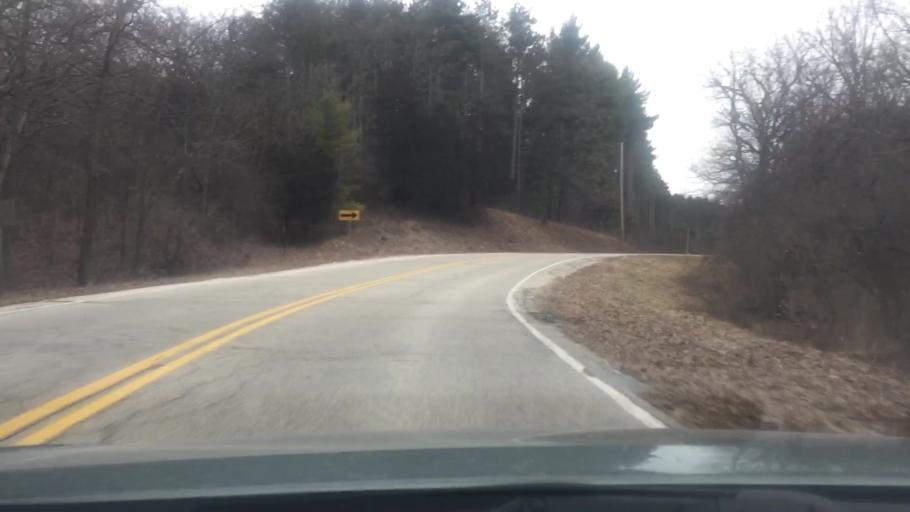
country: US
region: Wisconsin
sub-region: Waukesha County
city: North Prairie
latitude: 42.9427
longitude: -88.4499
